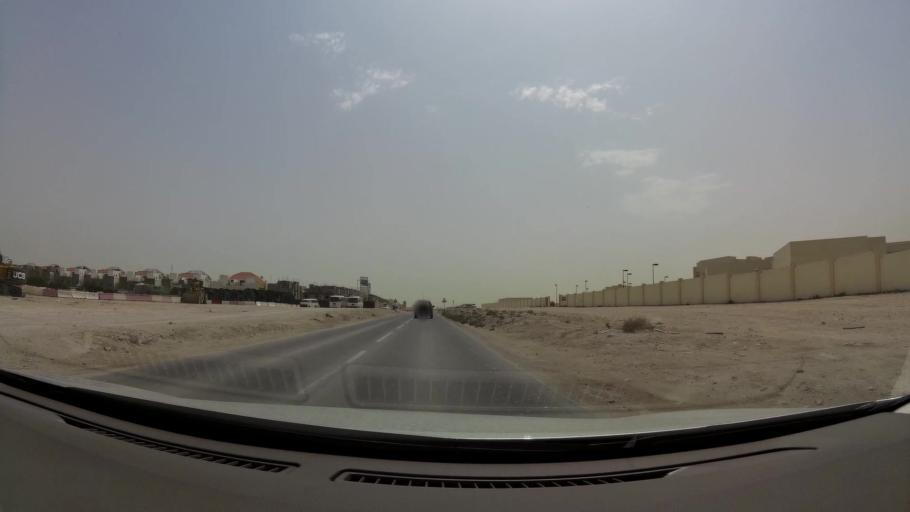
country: QA
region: Baladiyat ar Rayyan
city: Ar Rayyan
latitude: 25.2317
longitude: 51.4080
